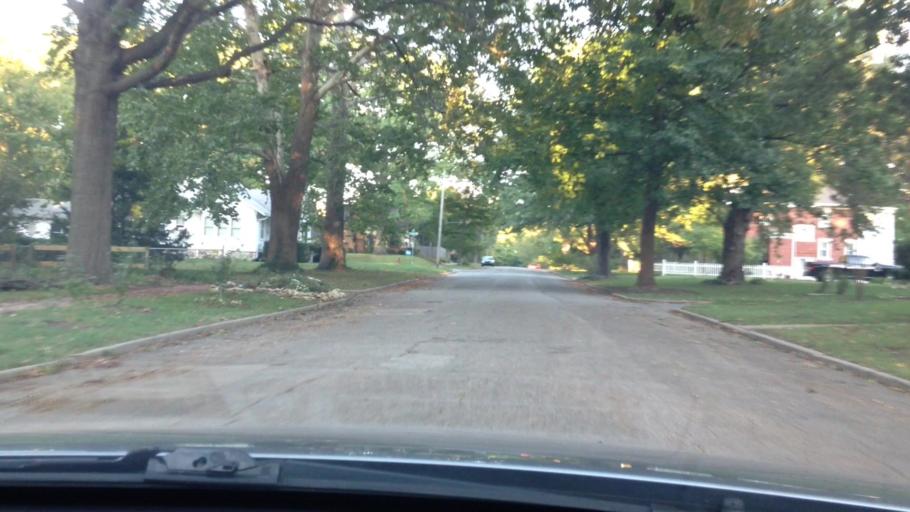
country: US
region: Kansas
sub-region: Leavenworth County
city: Leavenworth
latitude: 39.3020
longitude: -94.9232
